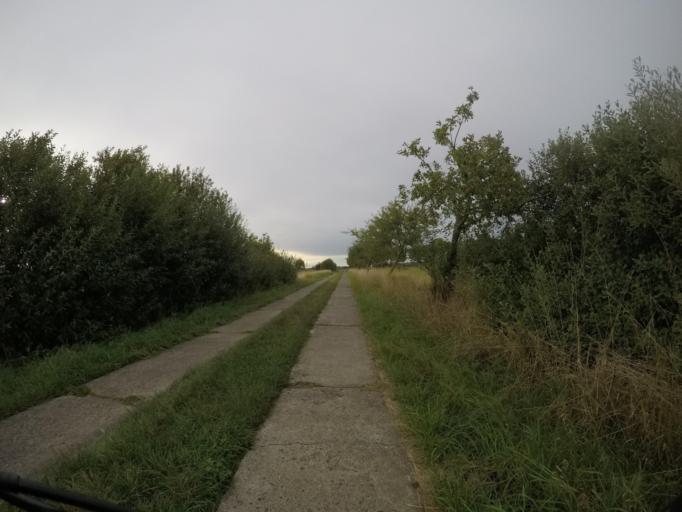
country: DE
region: Lower Saxony
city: Neu Darchau
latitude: 53.2745
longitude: 10.8648
